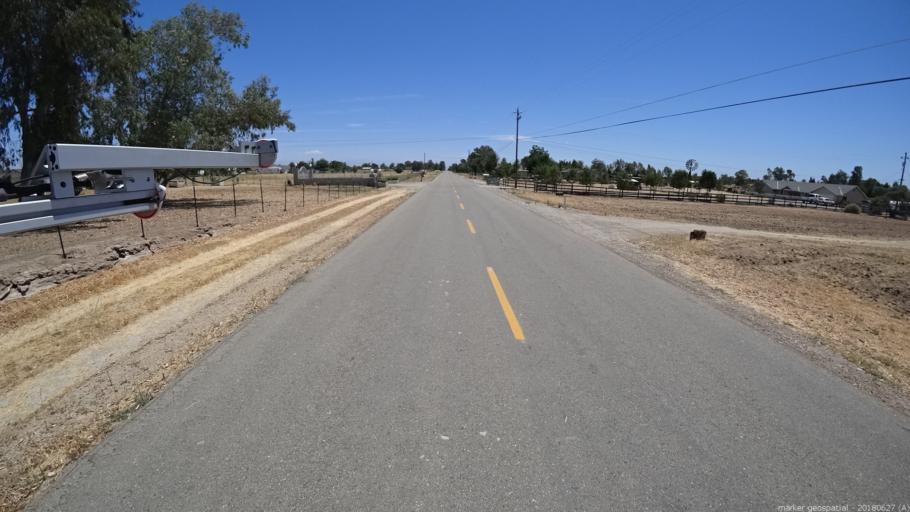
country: US
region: California
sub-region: Madera County
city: Bonadelle Ranchos-Madera Ranchos
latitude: 36.9448
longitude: -119.9183
